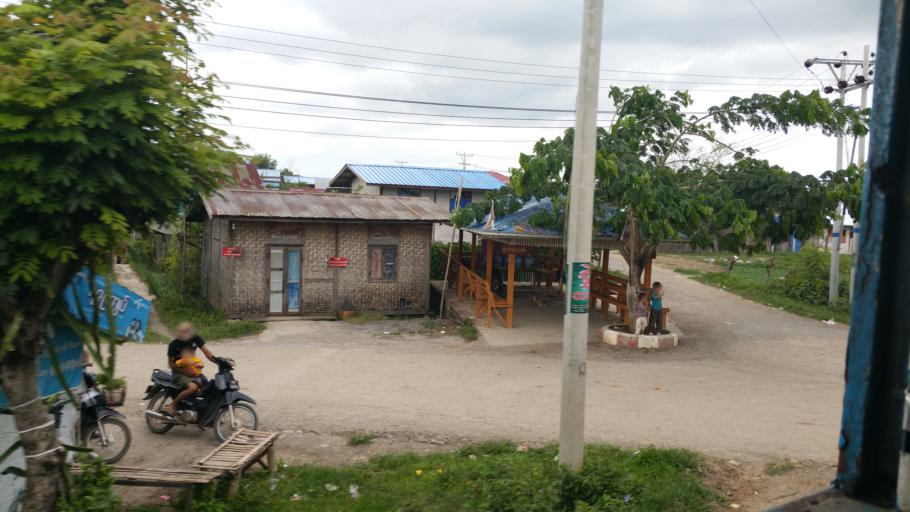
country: MM
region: Shan
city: Taunggyi
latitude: 20.7631
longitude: 96.9369
